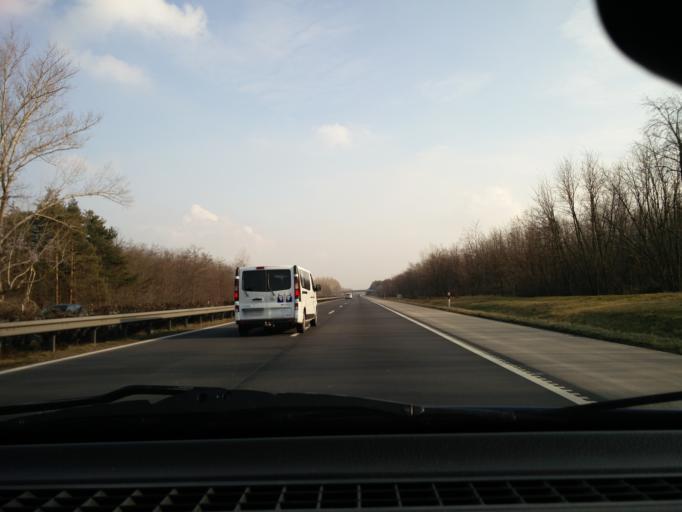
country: HU
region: Pest
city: Felsopakony
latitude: 47.3229
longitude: 19.2469
